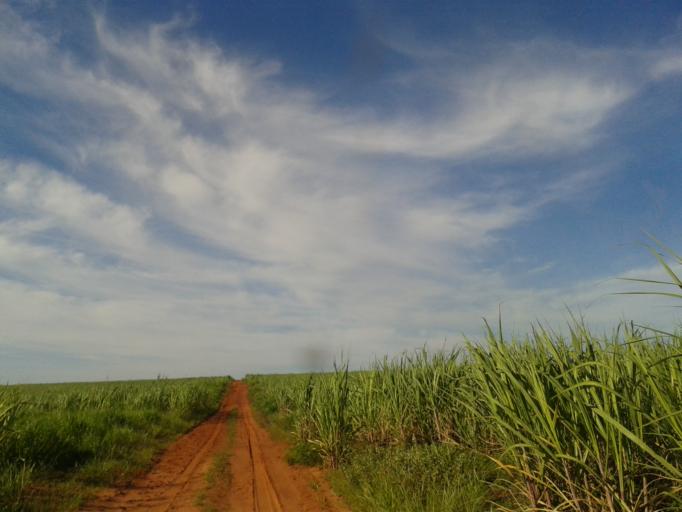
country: BR
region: Minas Gerais
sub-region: Santa Vitoria
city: Santa Vitoria
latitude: -19.1230
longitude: -50.0034
